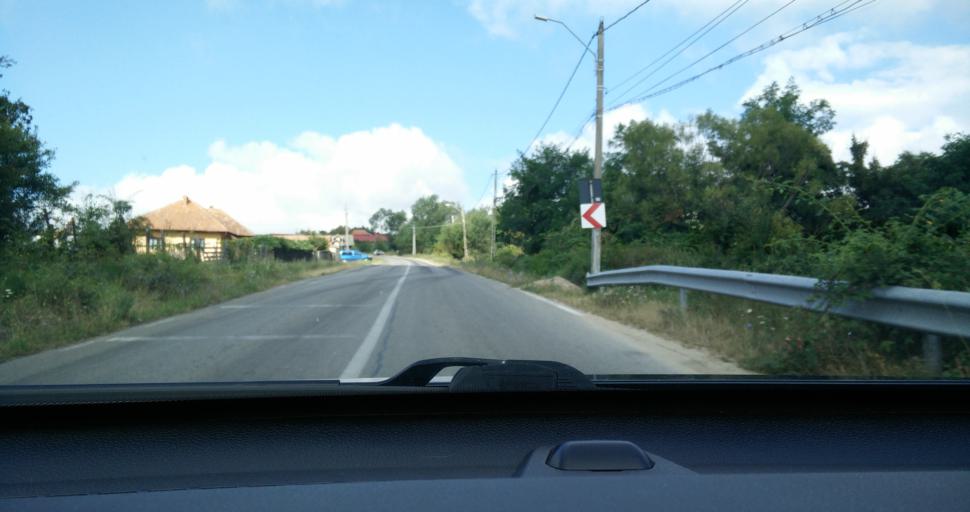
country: RO
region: Gorj
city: Novaci-Straini
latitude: 45.1784
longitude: 23.7030
